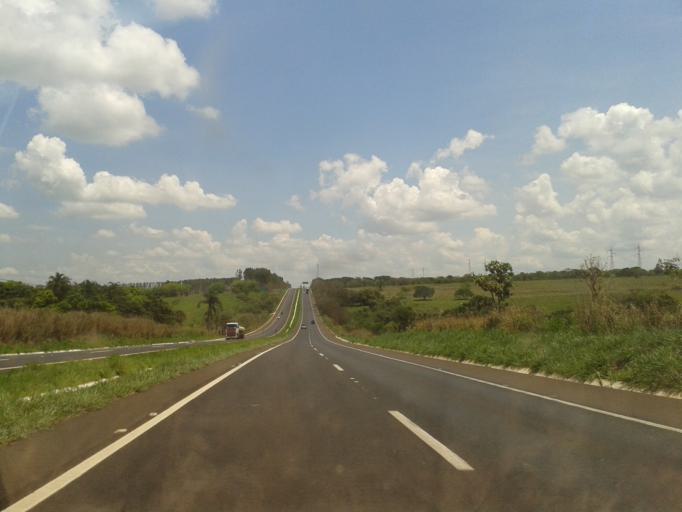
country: BR
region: Minas Gerais
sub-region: Uberlandia
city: Uberlandia
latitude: -18.8845
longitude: -48.4703
